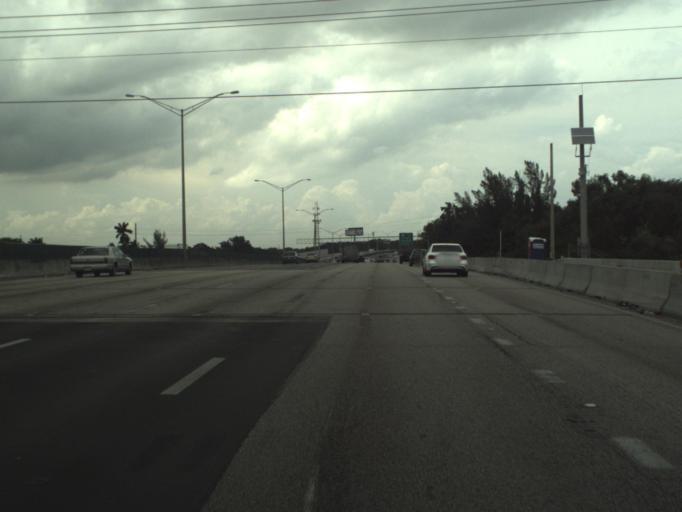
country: US
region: Florida
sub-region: Broward County
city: Hollywood
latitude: 26.0181
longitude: -80.1671
